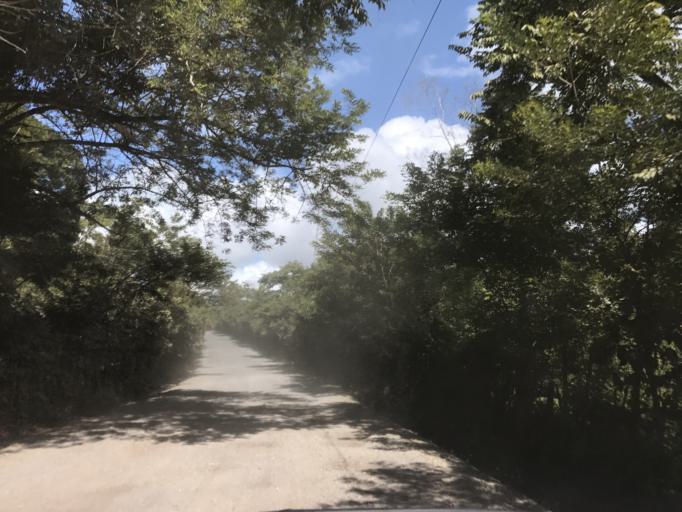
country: GT
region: Izabal
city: Morales
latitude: 15.6459
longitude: -89.0205
